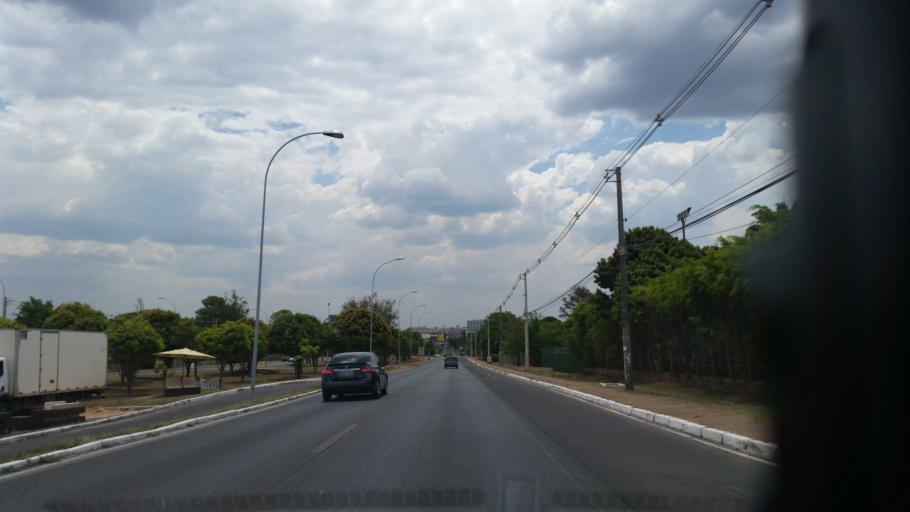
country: BR
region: Federal District
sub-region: Brasilia
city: Brasilia
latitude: -15.7248
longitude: -47.8763
